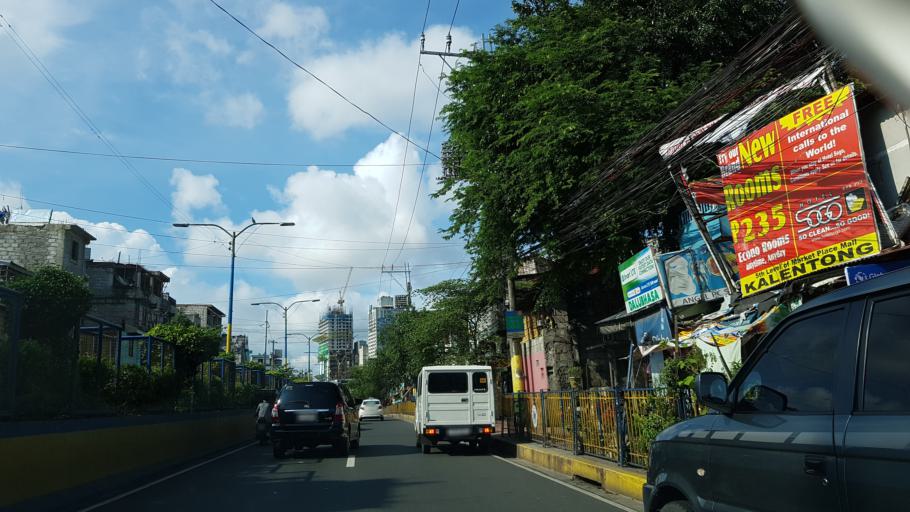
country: PH
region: Metro Manila
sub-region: Mandaluyong
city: Mandaluyong City
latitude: 14.5838
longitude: 121.0376
